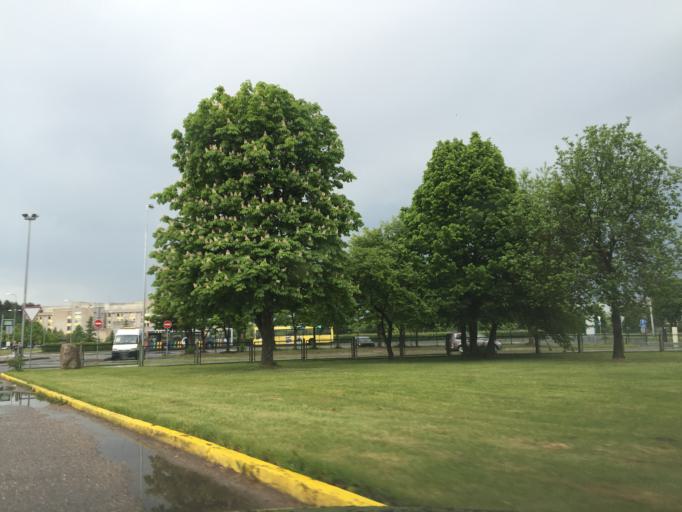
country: LT
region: Klaipedos apskritis
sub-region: Klaipeda
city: Klaipeda
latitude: 55.7539
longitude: 21.1293
